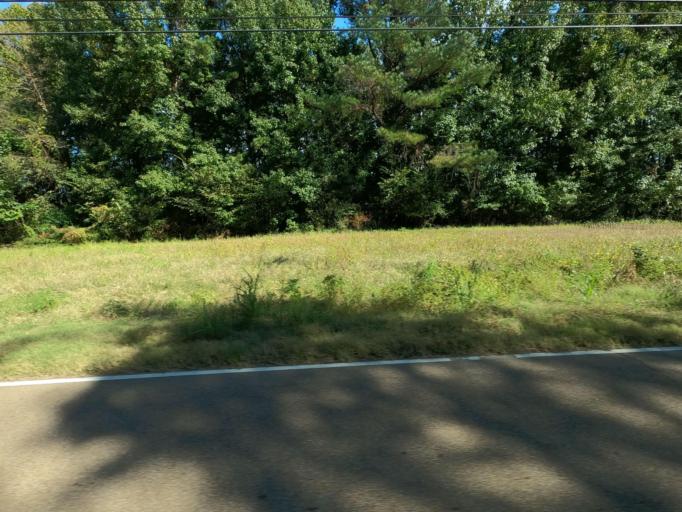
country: US
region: Tennessee
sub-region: Fayette County
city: Hickory Withe
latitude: 35.2308
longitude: -89.6500
